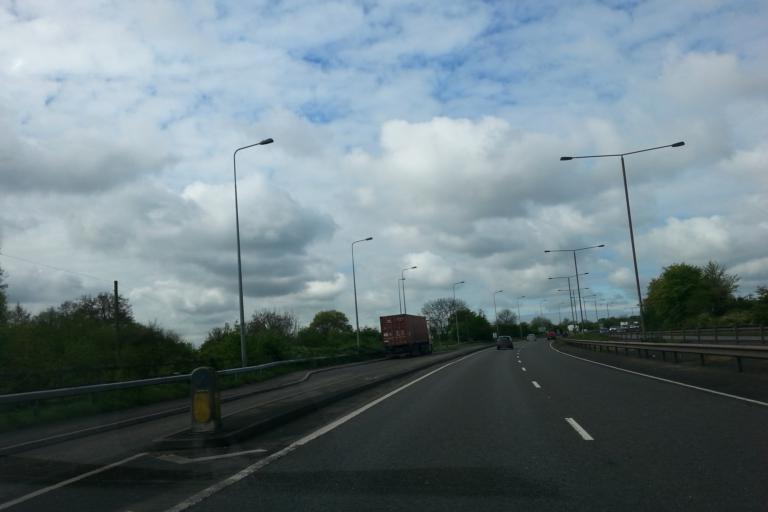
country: GB
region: England
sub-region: Derbyshire
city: Etwall
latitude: 52.8428
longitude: -1.5984
